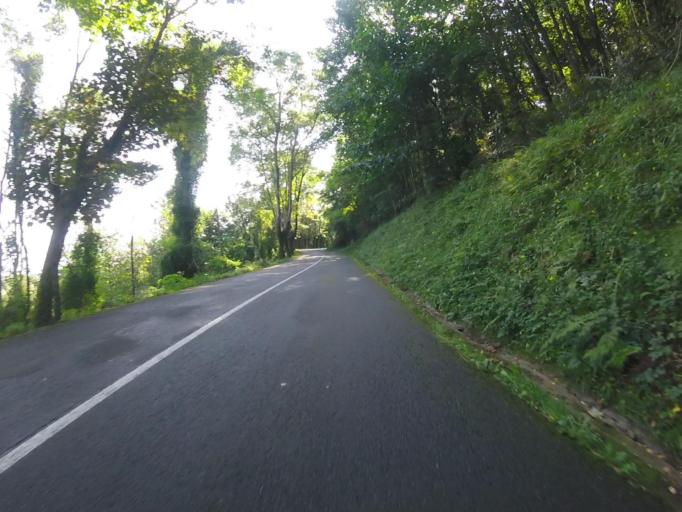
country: ES
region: Basque Country
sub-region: Provincia de Guipuzcoa
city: Irun
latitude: 43.3319
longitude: -1.7659
